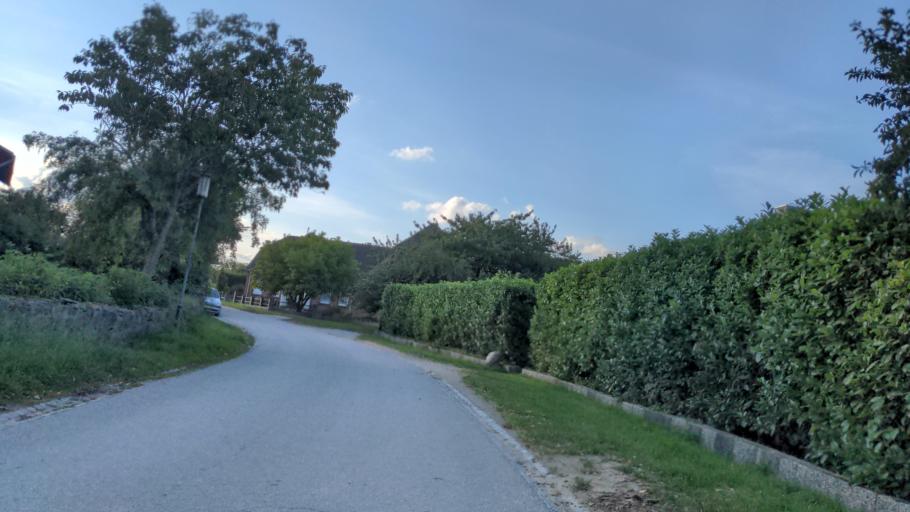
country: DE
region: Schleswig-Holstein
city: Ahrensbok
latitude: 53.9804
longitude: 10.6284
